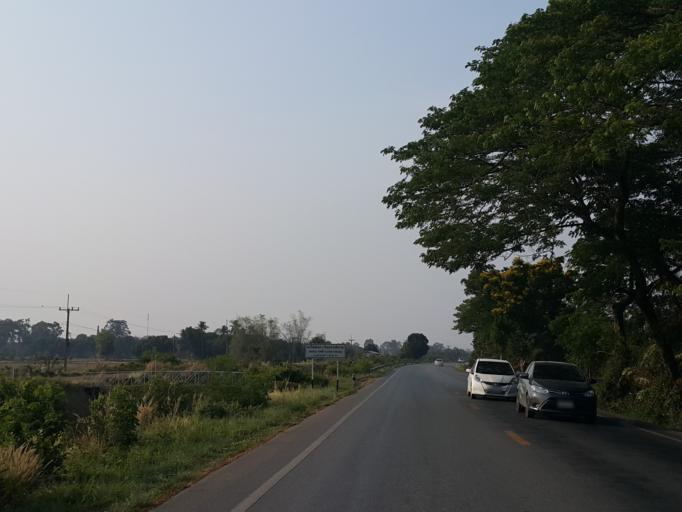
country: TH
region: Chai Nat
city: Sankhaburi
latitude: 15.0297
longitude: 100.1447
